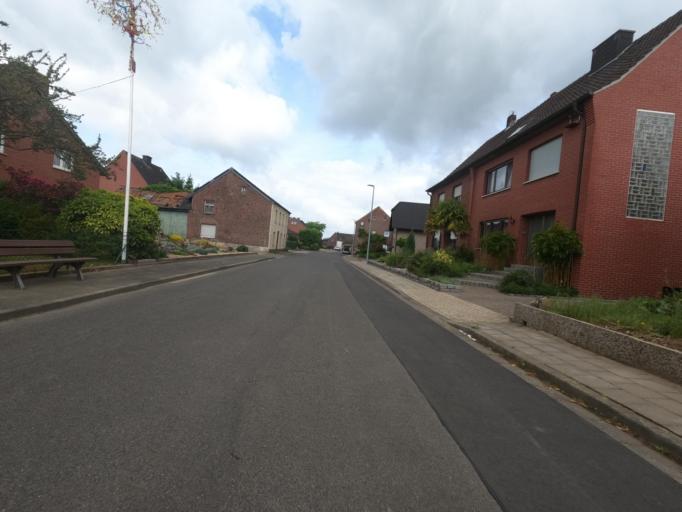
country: NL
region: Limburg
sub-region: Gemeente Roerdalen
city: Vlodrop
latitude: 51.1084
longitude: 6.1043
